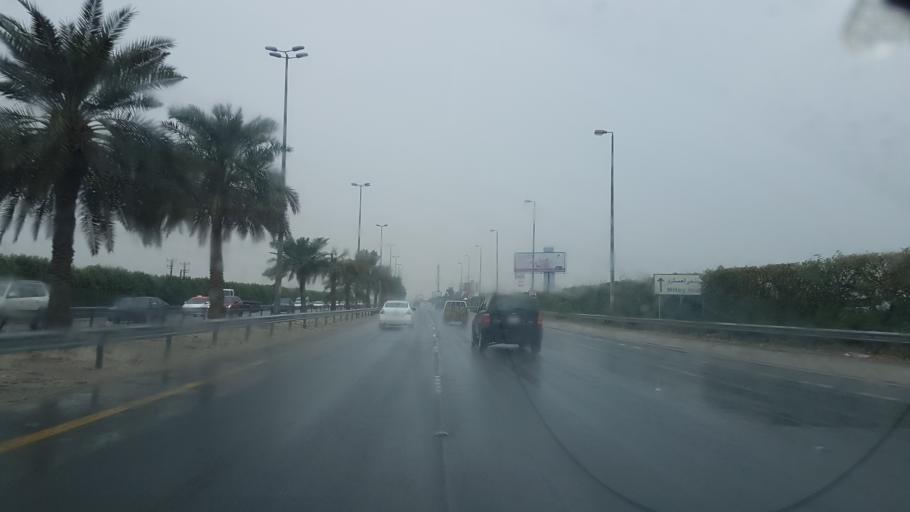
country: BH
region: Northern
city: Madinat `Isa
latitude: 26.1737
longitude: 50.5023
